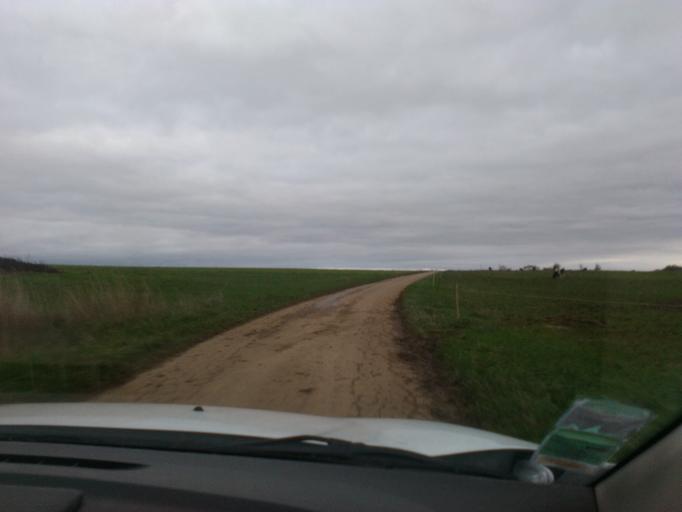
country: FR
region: Lorraine
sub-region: Departement des Vosges
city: Mirecourt
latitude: 48.2832
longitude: 6.1995
